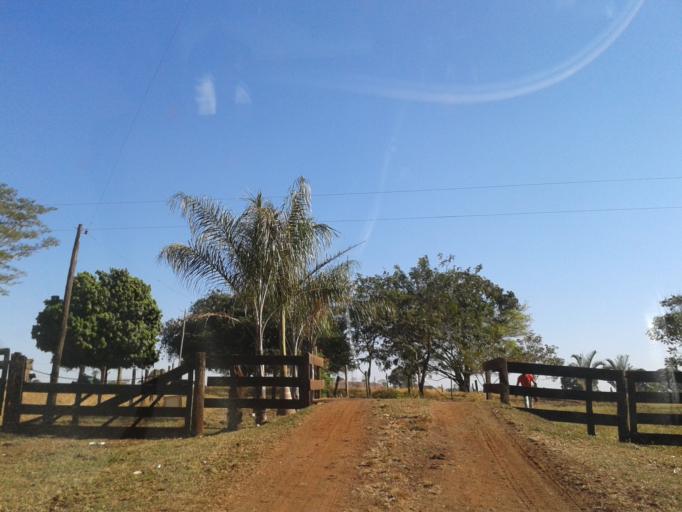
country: BR
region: Minas Gerais
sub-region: Santa Vitoria
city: Santa Vitoria
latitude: -19.0688
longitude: -49.9247
